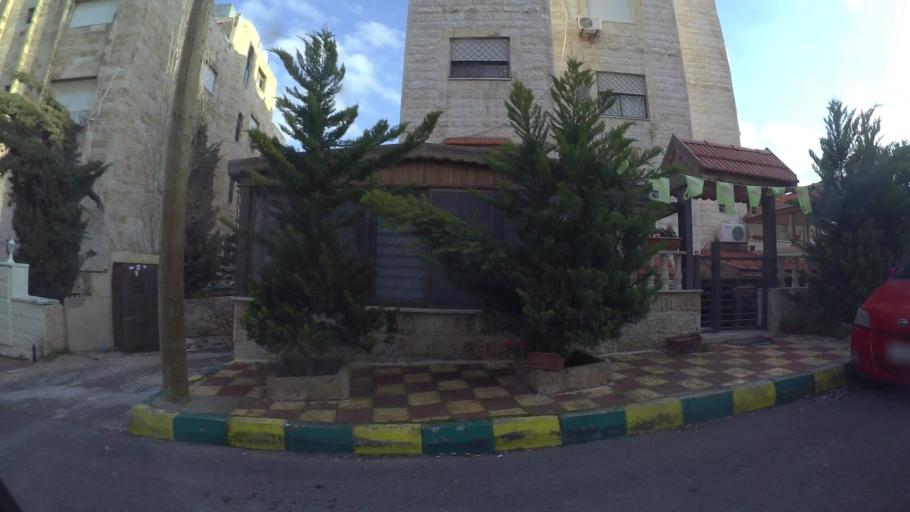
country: JO
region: Amman
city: Al Jubayhah
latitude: 32.0012
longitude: 35.8700
